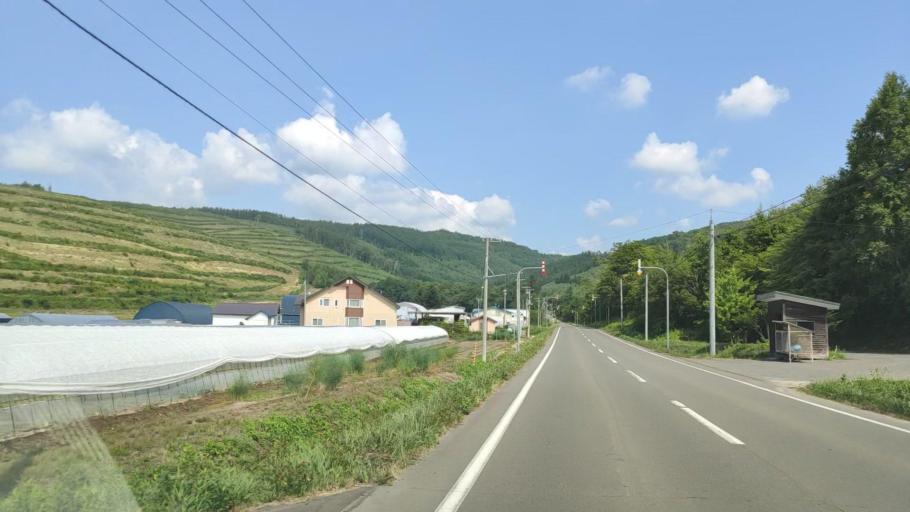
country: JP
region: Hokkaido
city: Shimo-furano
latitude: 43.4206
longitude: 142.4018
